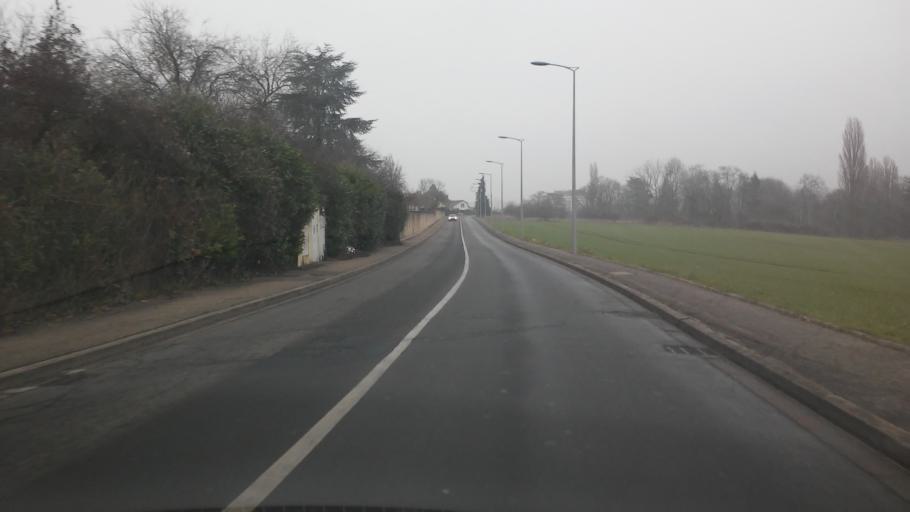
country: FR
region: Lorraine
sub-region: Departement de la Moselle
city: Montigny-les-Metz
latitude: 49.0884
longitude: 6.1711
